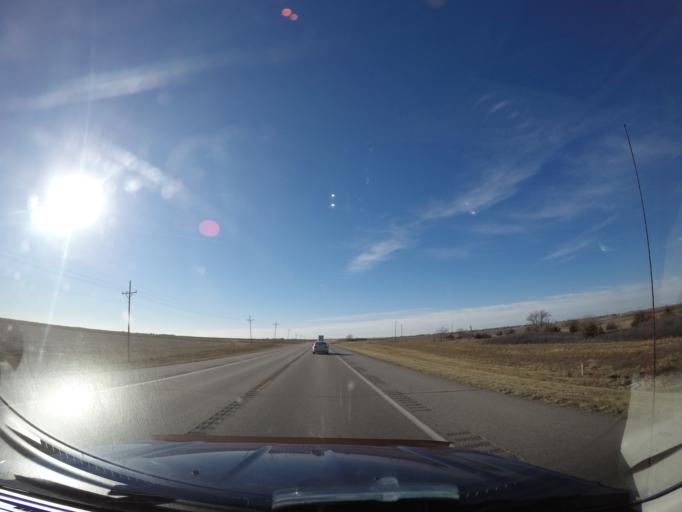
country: US
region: Kansas
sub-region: Marion County
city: Hillsboro
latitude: 38.3623
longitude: -97.2781
